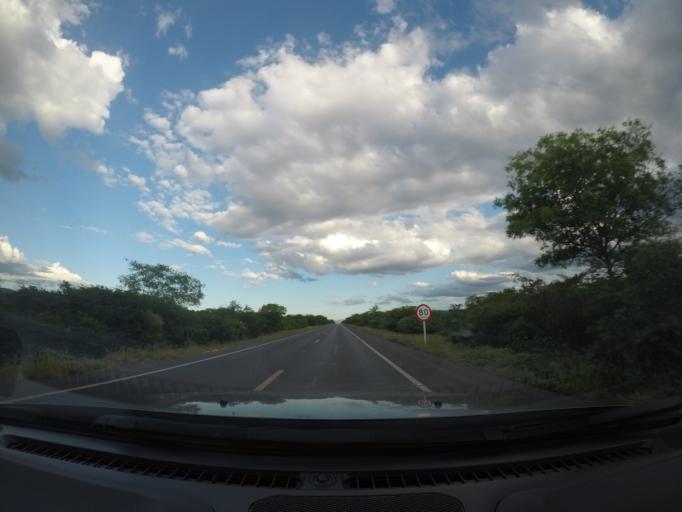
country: BR
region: Bahia
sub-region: Oliveira Dos Brejinhos
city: Beira Rio
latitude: -12.2780
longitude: -42.6948
